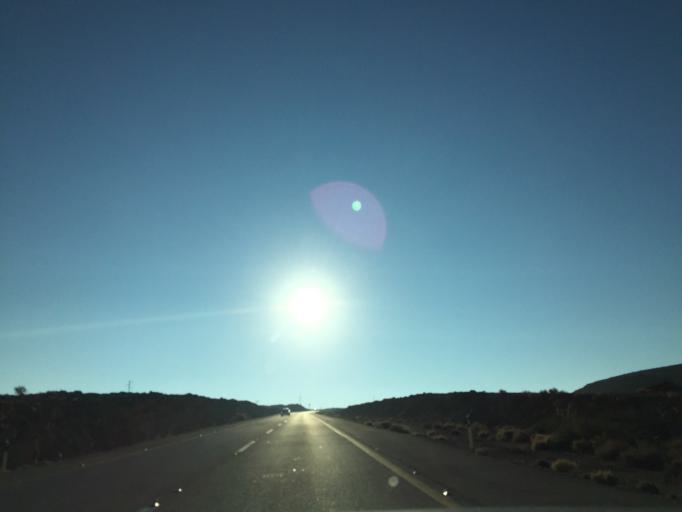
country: IL
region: Southern District
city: Mitzpe Ramon
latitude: 30.5264
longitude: 34.9331
